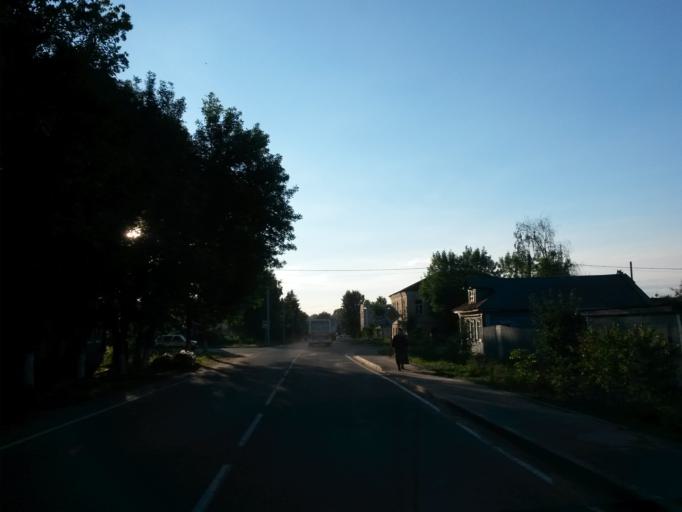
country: RU
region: Jaroslavl
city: Tutayev
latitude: 57.8728
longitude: 39.5257
